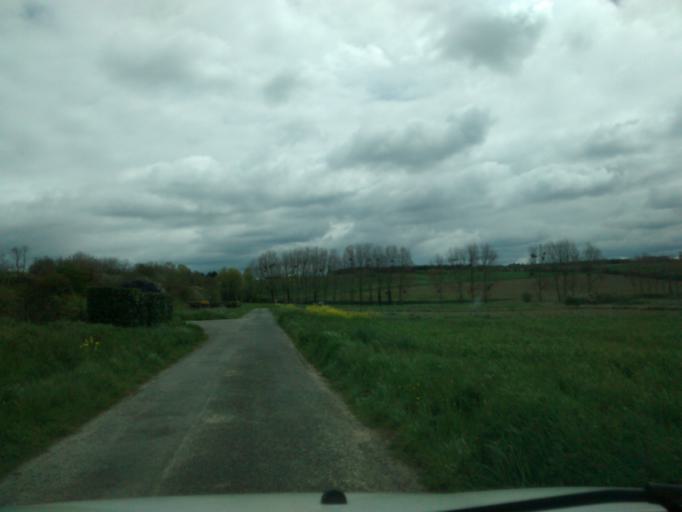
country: FR
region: Brittany
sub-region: Departement d'Ille-et-Vilaine
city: Saint-Jouan-des-Guerets
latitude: 48.5808
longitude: -1.9569
